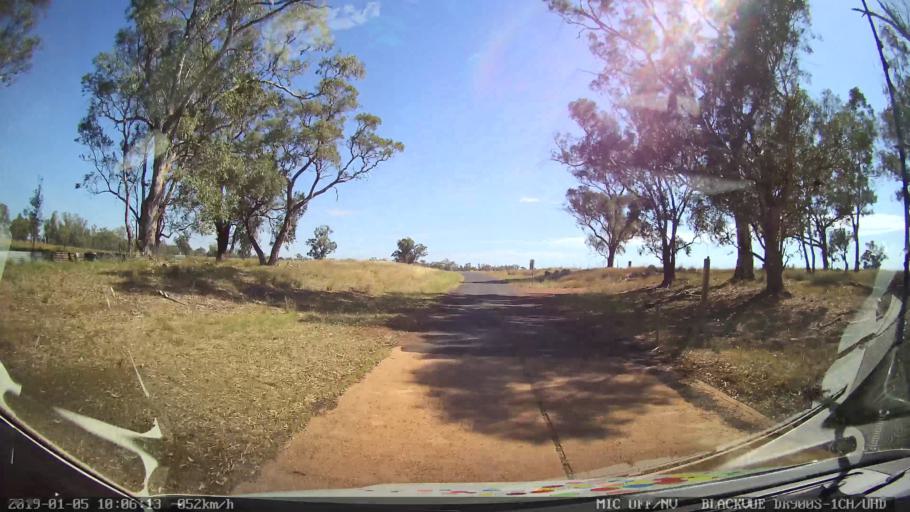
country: AU
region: New South Wales
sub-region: Gilgandra
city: Gilgandra
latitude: -31.6599
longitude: 148.8692
